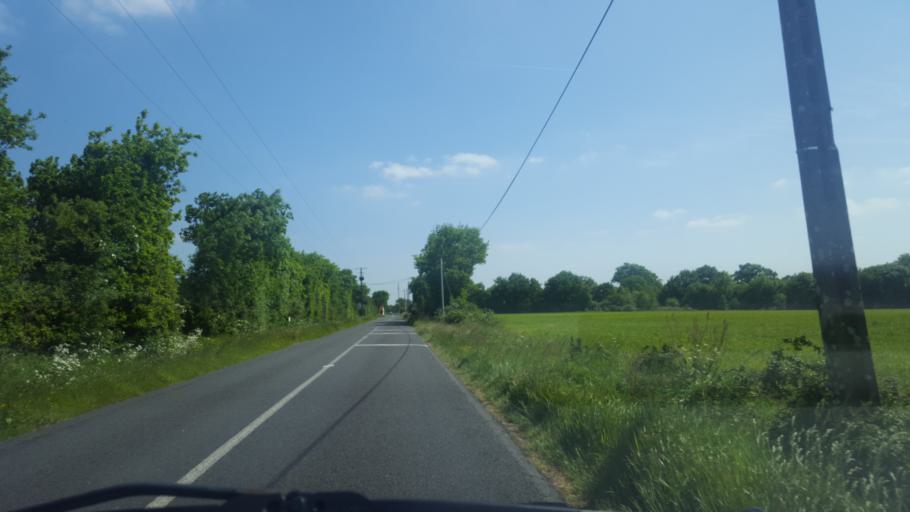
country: FR
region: Pays de la Loire
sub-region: Departement de la Loire-Atlantique
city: La Limouziniere
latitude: 47.0317
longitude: -1.5772
